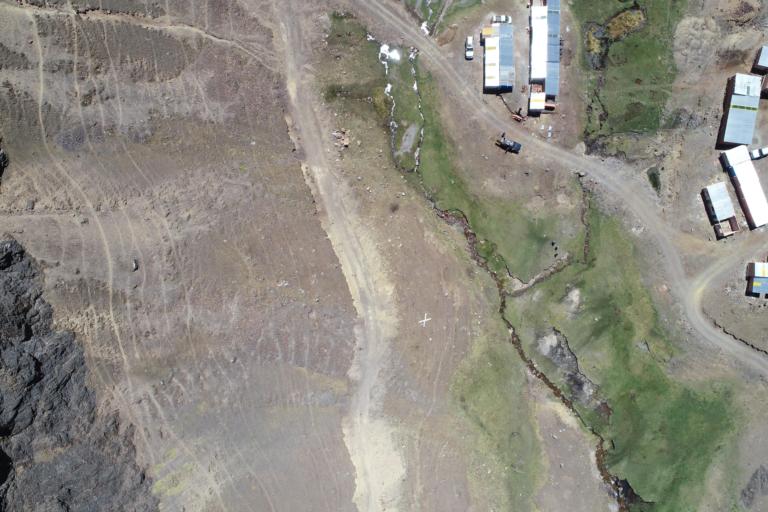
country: BO
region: La Paz
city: La Paz
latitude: -16.6205
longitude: -67.8286
